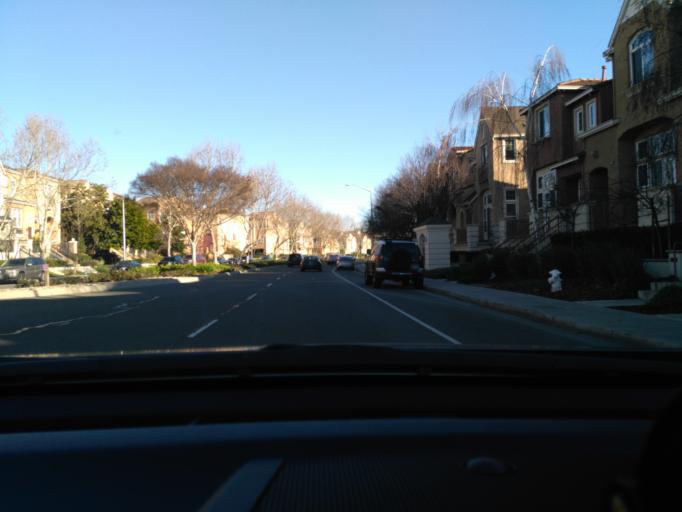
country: US
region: California
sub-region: Santa Clara County
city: Santa Clara
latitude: 37.4013
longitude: -121.9512
